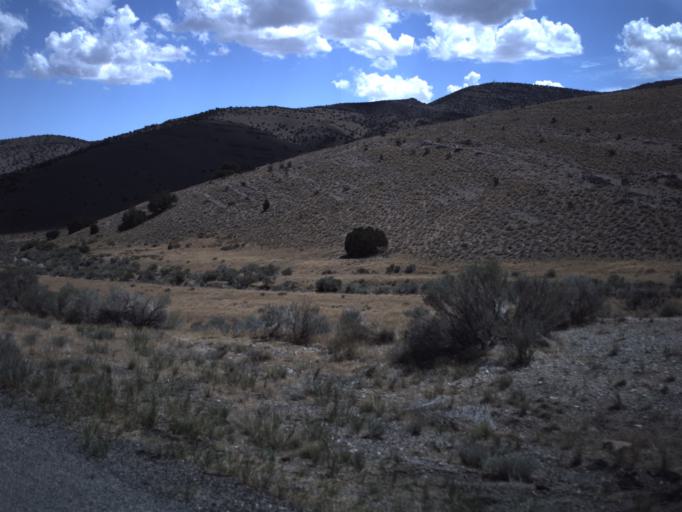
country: US
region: Utah
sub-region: Beaver County
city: Milford
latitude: 39.0775
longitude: -113.6200
